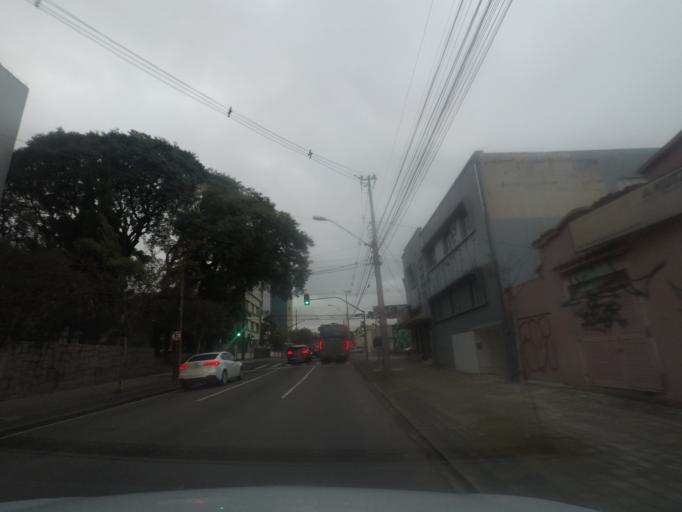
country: BR
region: Parana
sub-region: Curitiba
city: Curitiba
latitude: -25.4287
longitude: -49.2538
